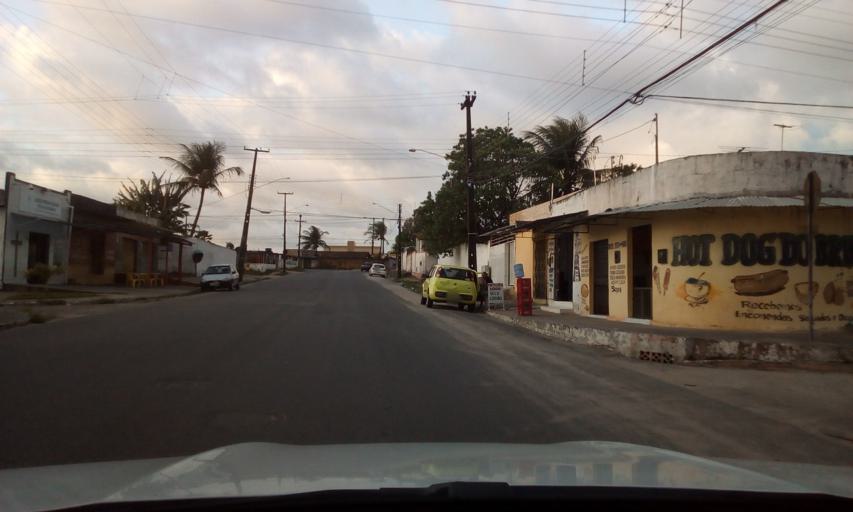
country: BR
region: Paraiba
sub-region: Joao Pessoa
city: Joao Pessoa
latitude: -7.1803
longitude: -34.8867
